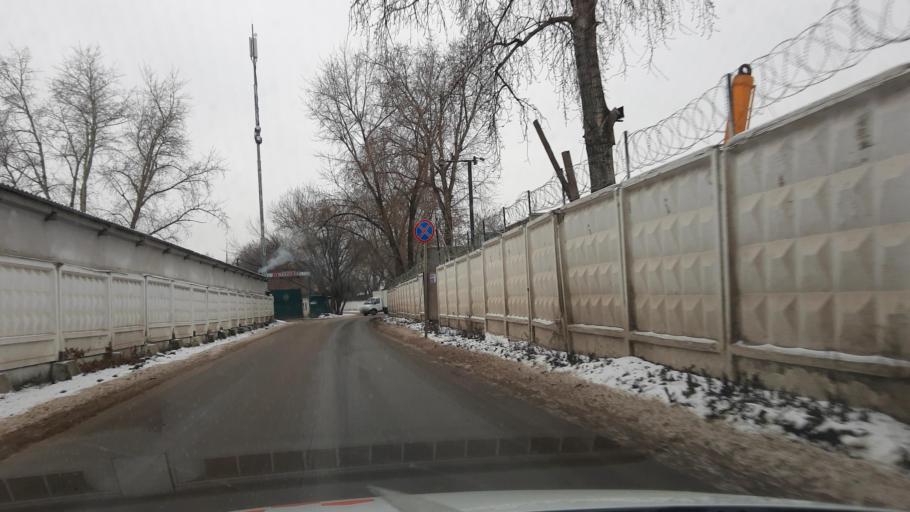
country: RU
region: Moscow
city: Lyublino
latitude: 55.6703
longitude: 37.7333
